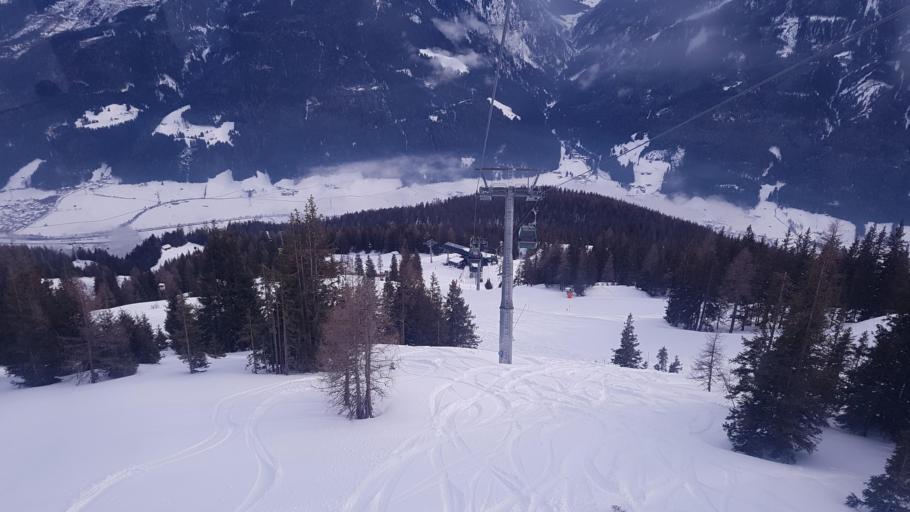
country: AT
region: Salzburg
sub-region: Politischer Bezirk Zell am See
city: Neukirchen am Grossvenediger
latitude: 47.2755
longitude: 12.3004
